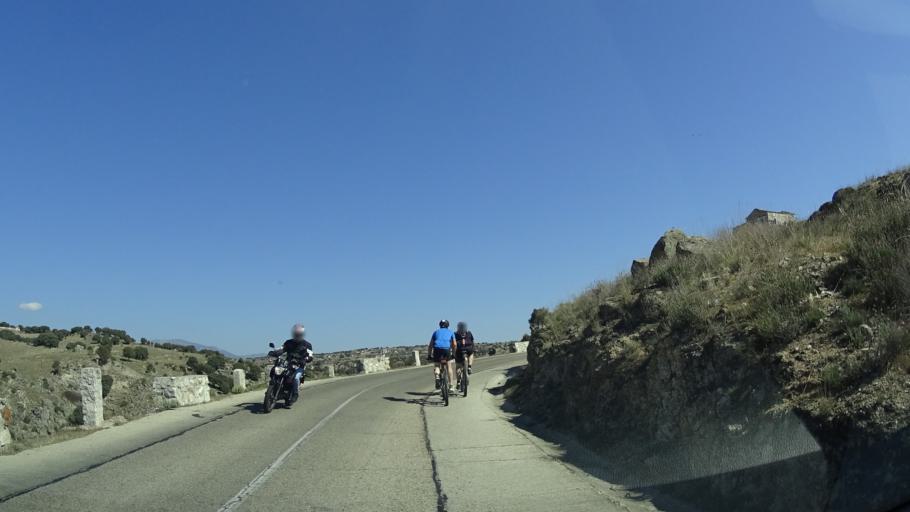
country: ES
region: Madrid
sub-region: Provincia de Madrid
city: Colmenar Viejo
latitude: 40.6480
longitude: -3.8079
